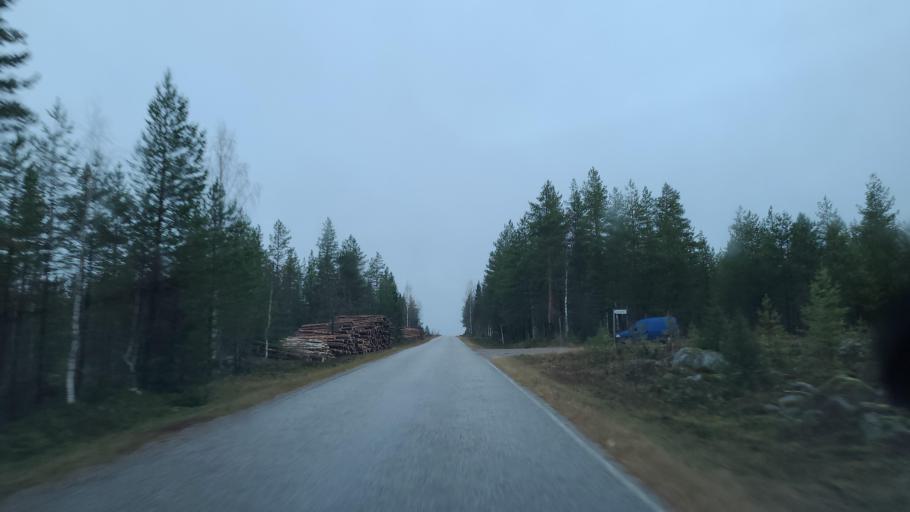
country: FI
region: Lapland
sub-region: Kemi-Tornio
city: Simo
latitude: 65.9082
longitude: 25.2032
